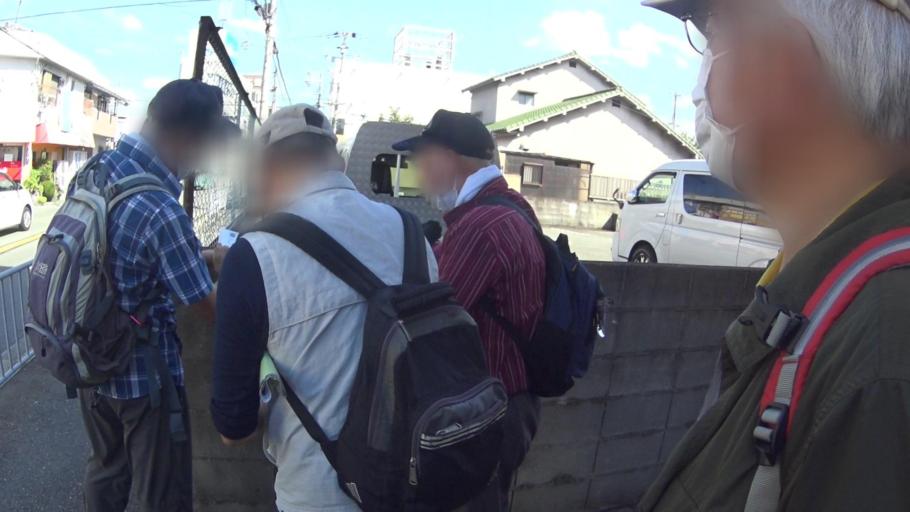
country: JP
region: Ehime
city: Kihoku-cho
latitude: 33.3882
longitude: 132.8387
